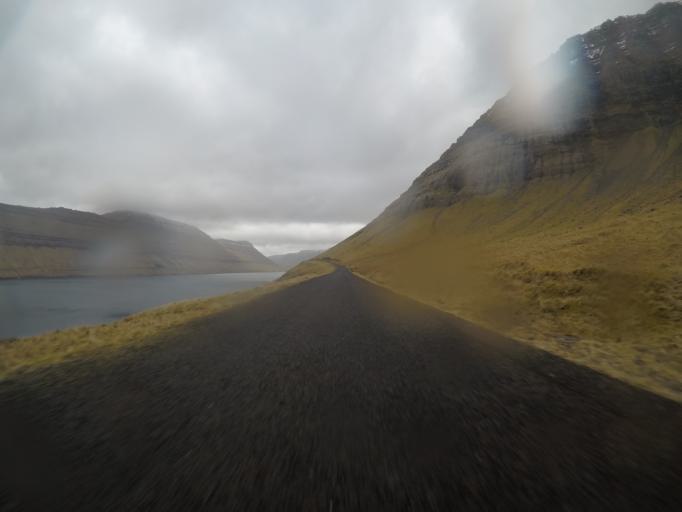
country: FO
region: Nordoyar
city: Klaksvik
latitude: 62.3340
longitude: -6.5761
